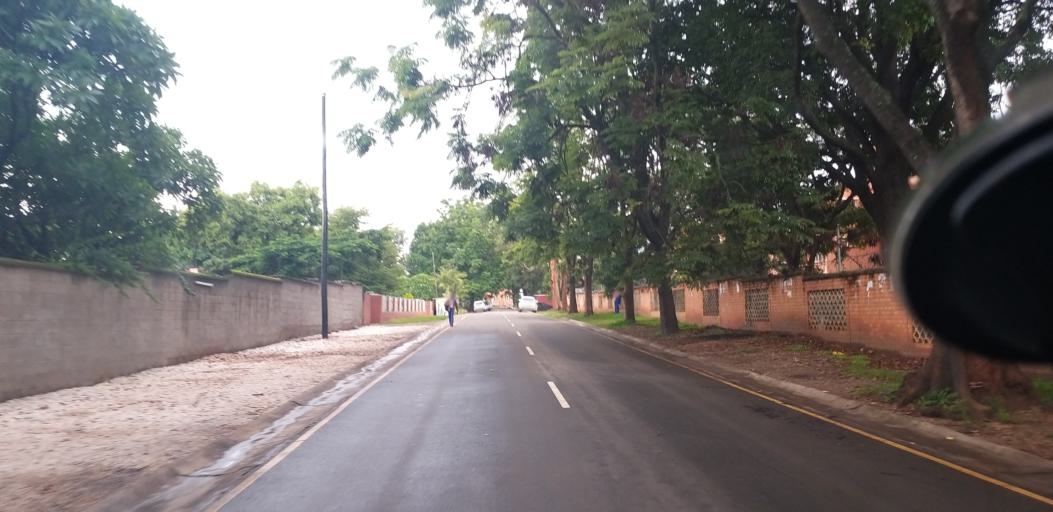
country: ZM
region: Lusaka
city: Lusaka
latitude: -15.4154
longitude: 28.2975
